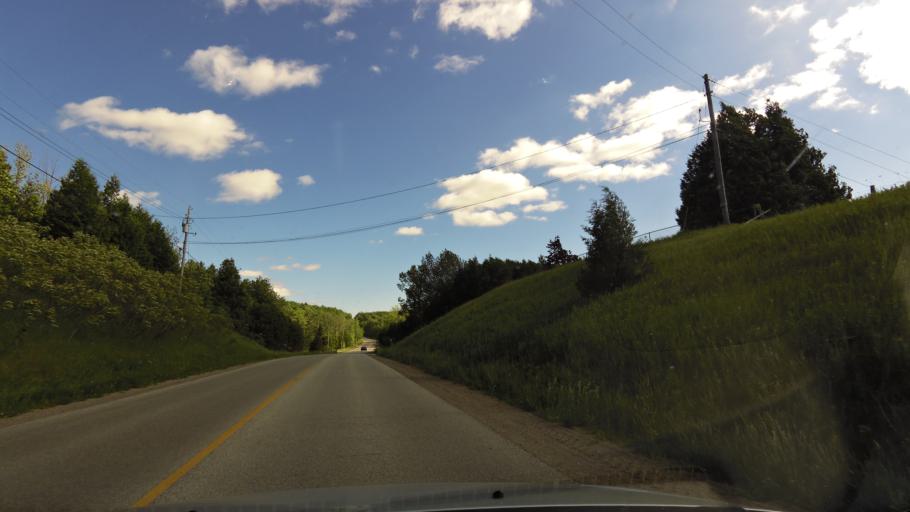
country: CA
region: Ontario
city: Bradford West Gwillimbury
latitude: 44.1756
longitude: -79.6189
